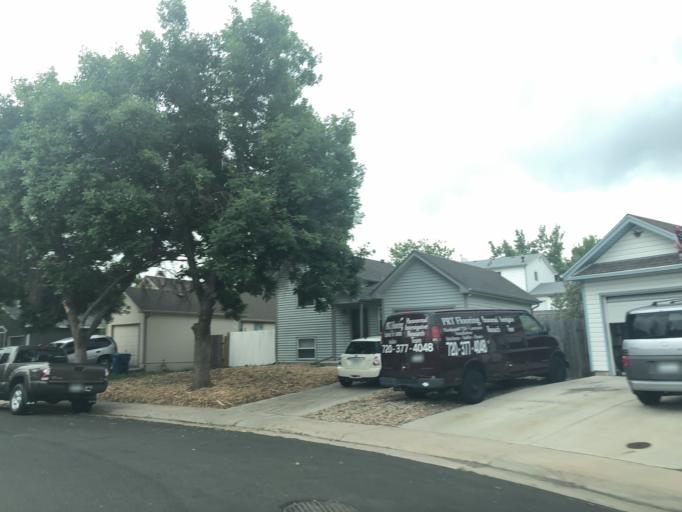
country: US
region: Colorado
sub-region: Arapahoe County
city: Dove Valley
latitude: 39.6274
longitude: -104.7848
